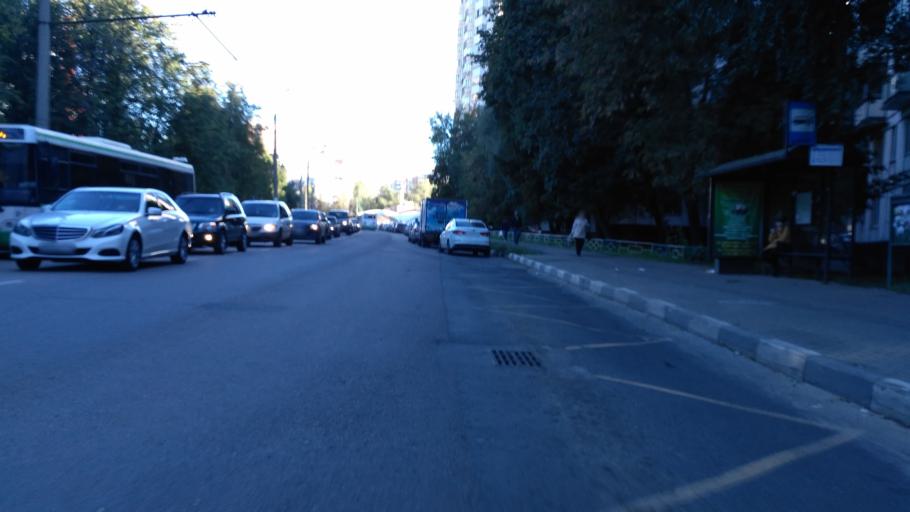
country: RU
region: Moscow
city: Likhobory
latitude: 55.8598
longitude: 37.5627
